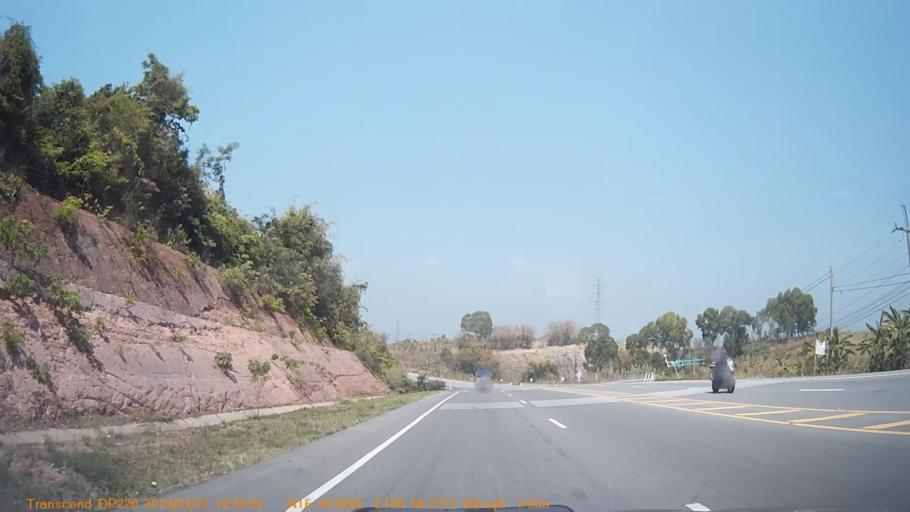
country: TH
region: Phetchabun
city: Khao Kho
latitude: 16.8263
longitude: 100.9365
